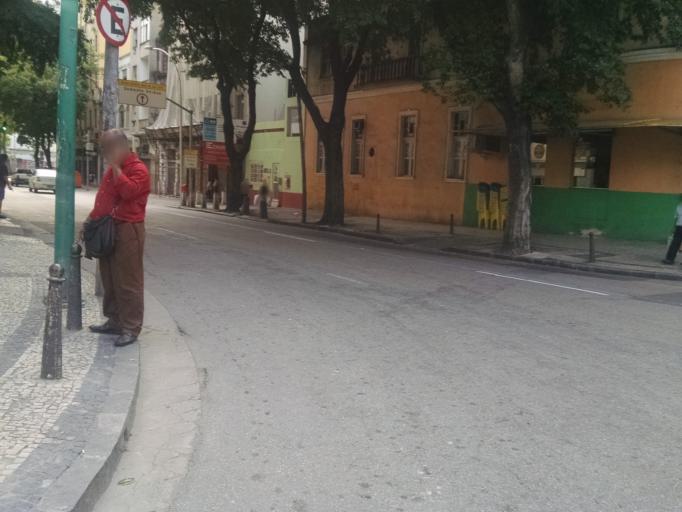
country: BR
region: Rio de Janeiro
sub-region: Rio De Janeiro
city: Rio de Janeiro
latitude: -22.9130
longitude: -43.1912
